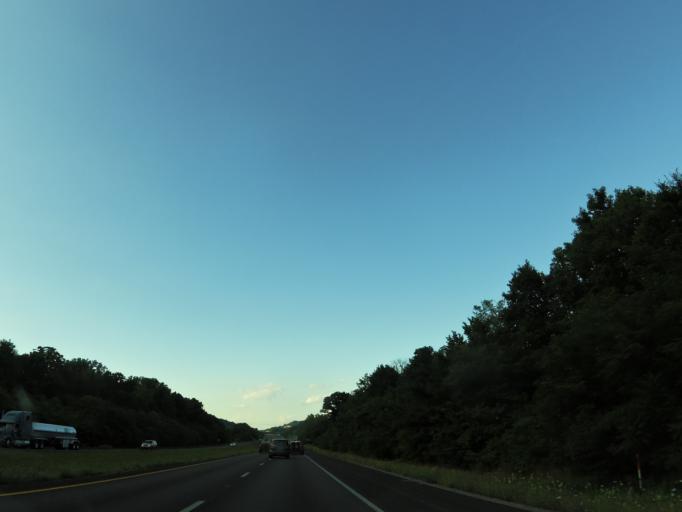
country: US
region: Tennessee
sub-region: Williamson County
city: Thompson's Station
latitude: 35.8031
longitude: -86.8522
